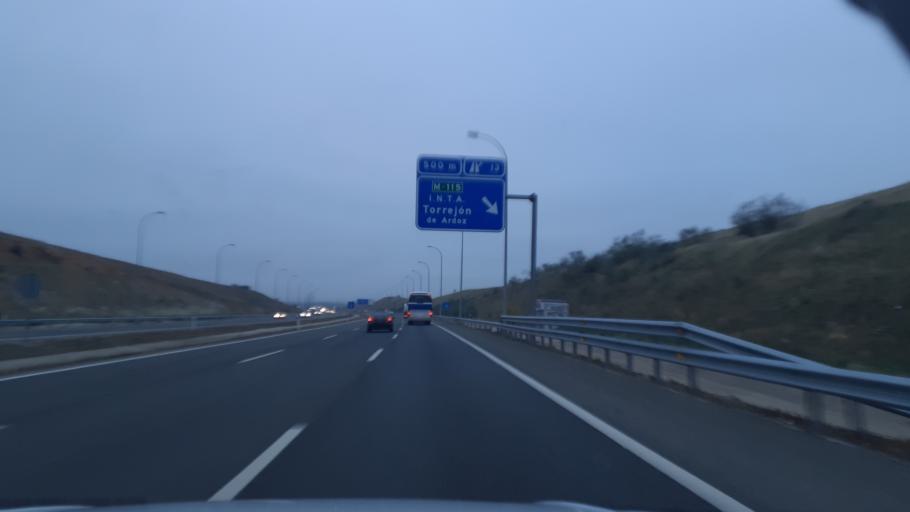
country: ES
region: Madrid
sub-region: Provincia de Madrid
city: Paracuellos de Jarama
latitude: 40.4909
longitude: -3.4963
